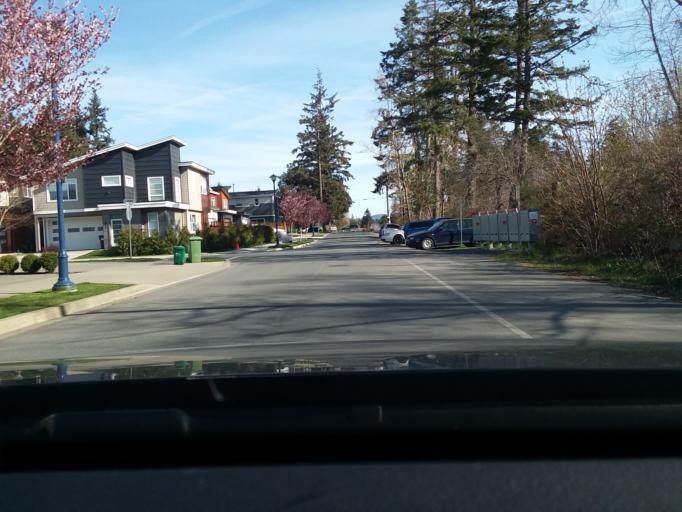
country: CA
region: British Columbia
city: Langford
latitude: 48.4280
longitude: -123.5318
